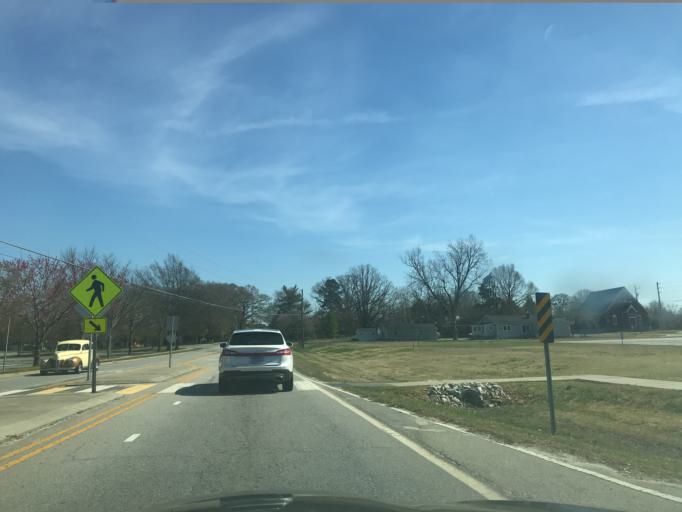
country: US
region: North Carolina
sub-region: Wake County
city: Fuquay-Varina
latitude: 35.5976
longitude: -78.7994
